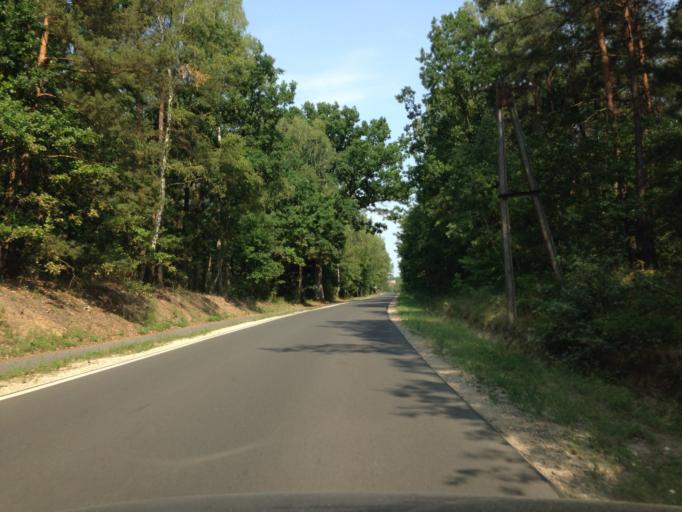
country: PL
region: Kujawsko-Pomorskie
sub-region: Powiat golubsko-dobrzynski
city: Golub-Dobrzyn
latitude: 53.0908
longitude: 19.0370
